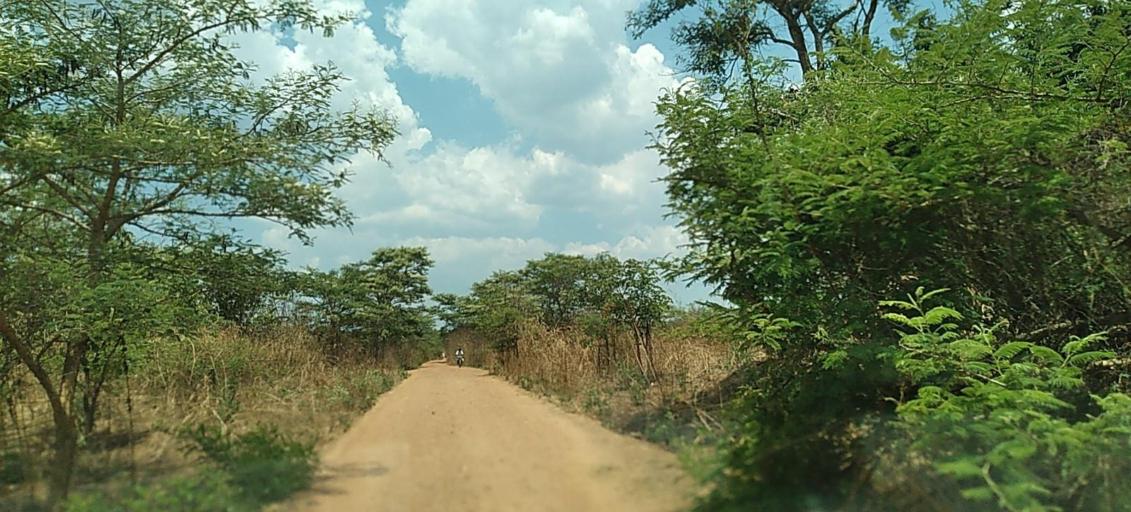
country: ZM
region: Copperbelt
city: Luanshya
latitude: -13.3728
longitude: 28.4205
